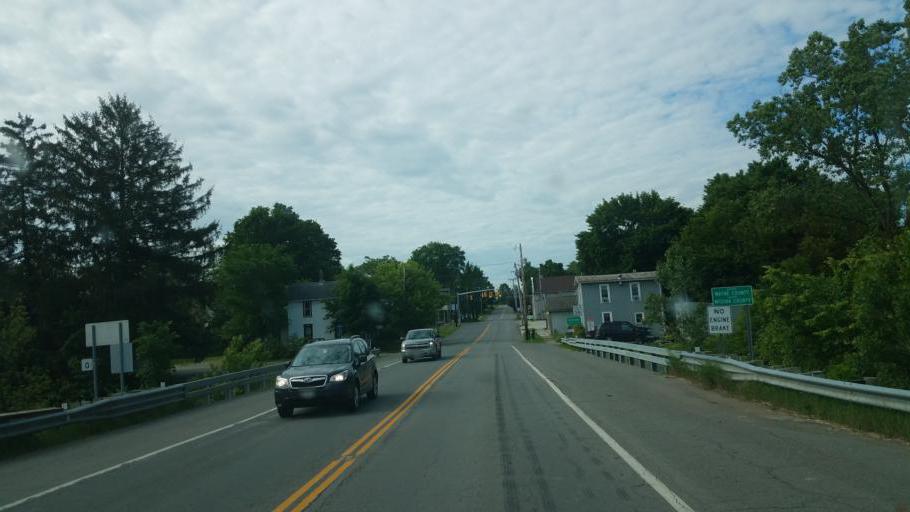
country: US
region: Ohio
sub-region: Medina County
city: Lodi
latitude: 40.9904
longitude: -81.9948
